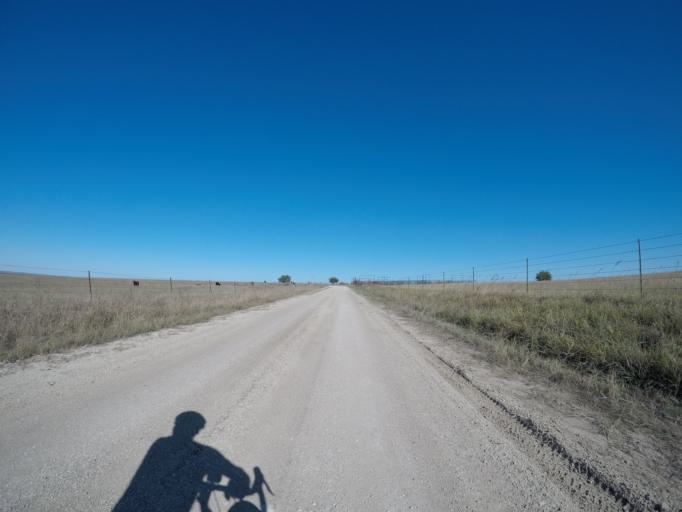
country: US
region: Kansas
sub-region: Wabaunsee County
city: Alma
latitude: 38.9187
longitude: -96.3882
